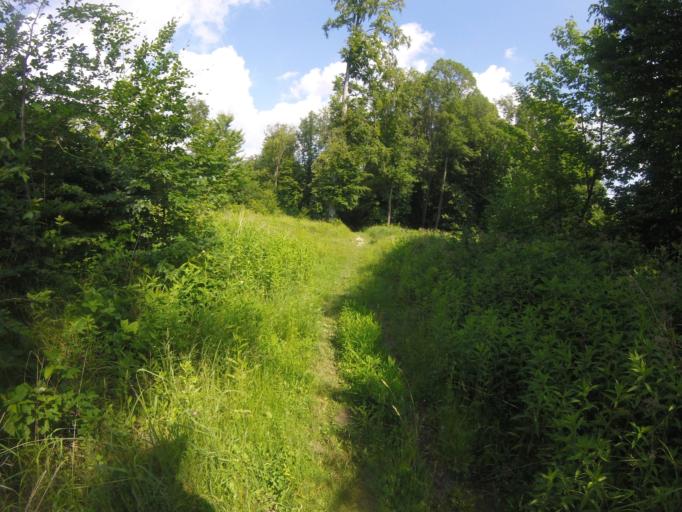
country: HU
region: Veszprem
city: Cseteny
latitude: 47.2750
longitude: 18.0353
